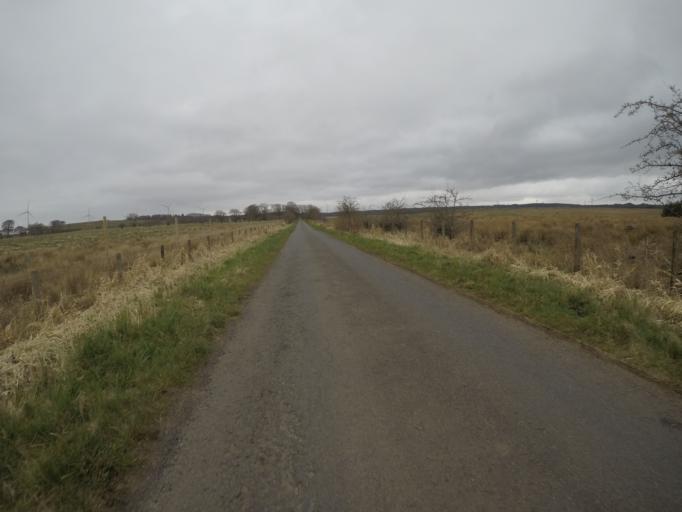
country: GB
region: Scotland
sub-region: East Ayrshire
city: Galston
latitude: 55.6631
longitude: -4.3701
